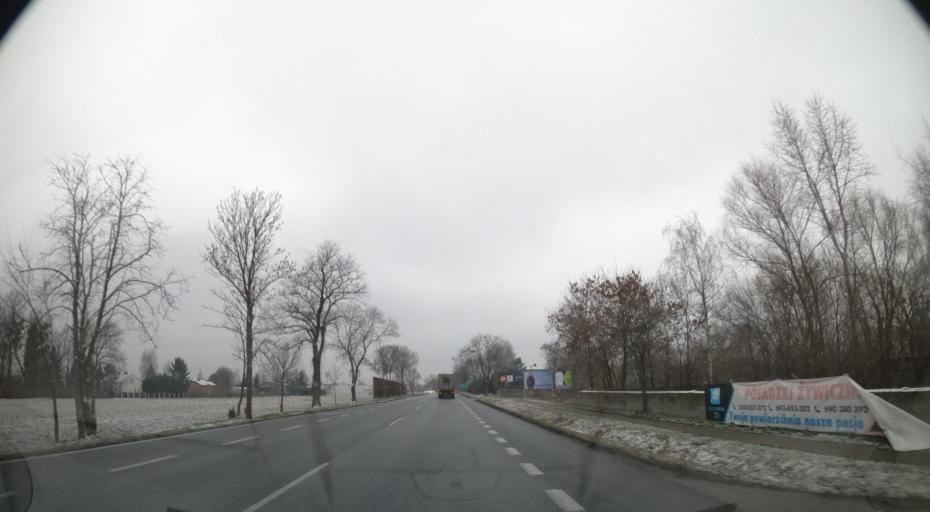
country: PL
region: Masovian Voivodeship
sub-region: Powiat sochaczewski
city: Sochaczew
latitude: 52.2262
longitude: 20.2732
